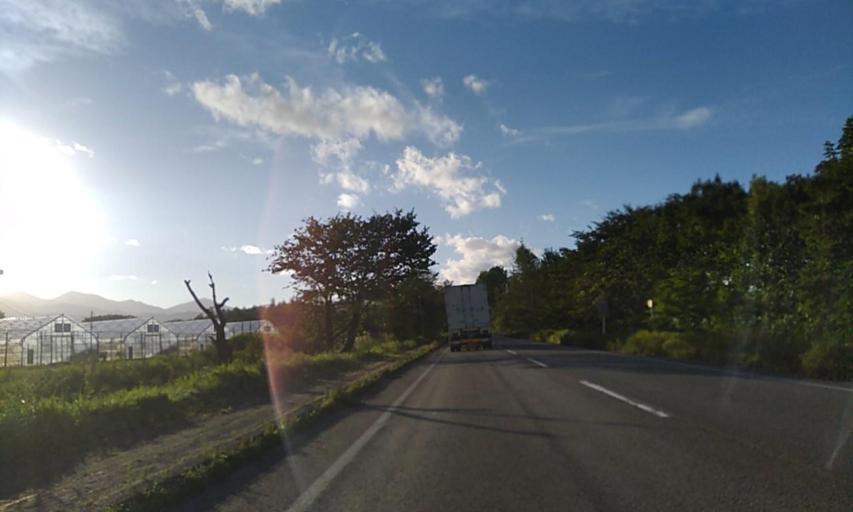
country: JP
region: Hokkaido
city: Otofuke
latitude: 42.9526
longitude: 142.9258
